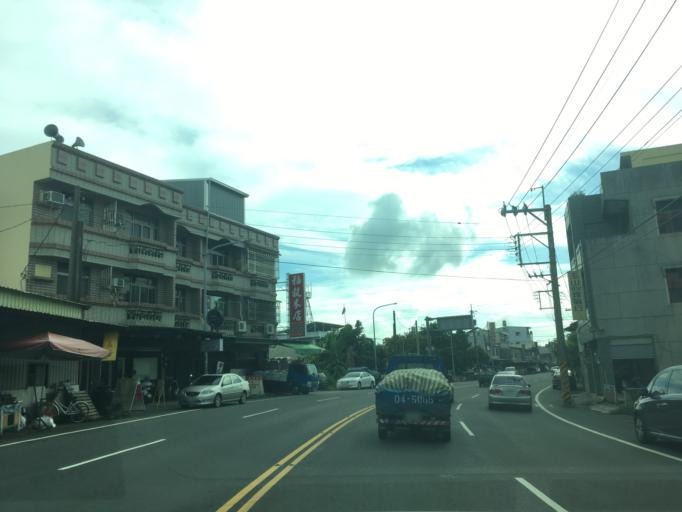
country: TW
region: Taiwan
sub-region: Chiayi
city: Jiayi Shi
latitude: 23.4411
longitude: 120.5342
